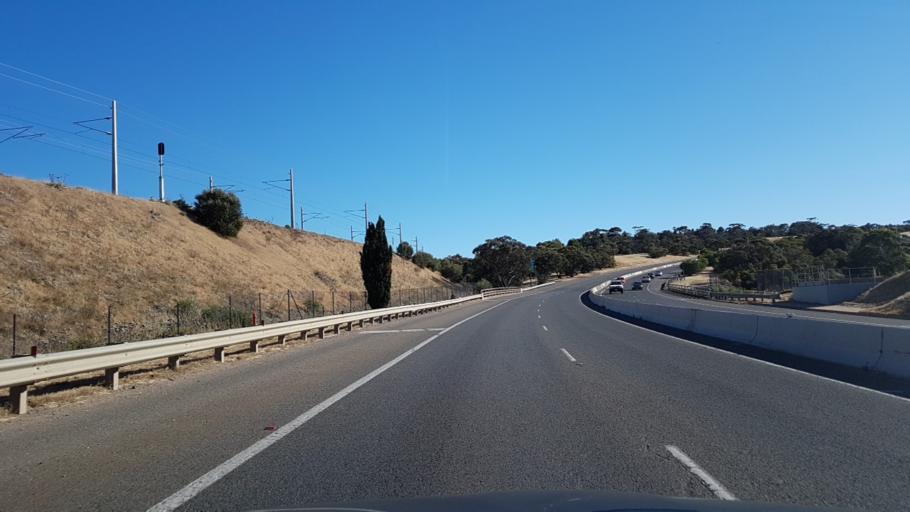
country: AU
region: South Australia
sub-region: Onkaparinga
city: Reynella
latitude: -35.0901
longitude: 138.4968
